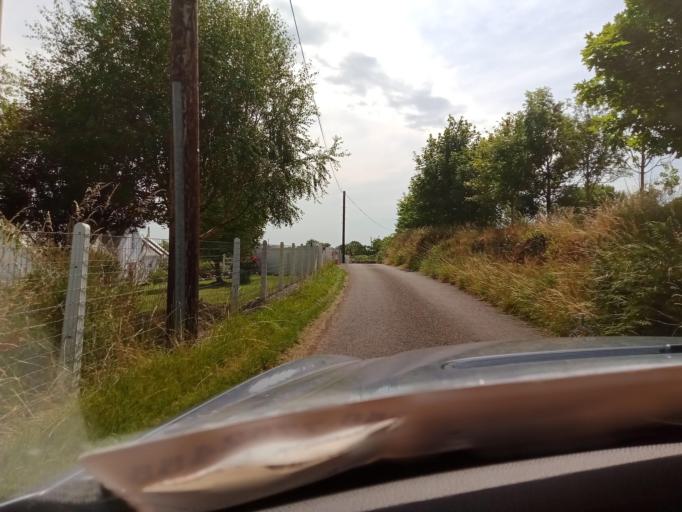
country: IE
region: Leinster
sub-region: Kilkenny
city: Mooncoin
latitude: 52.2634
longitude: -7.2062
